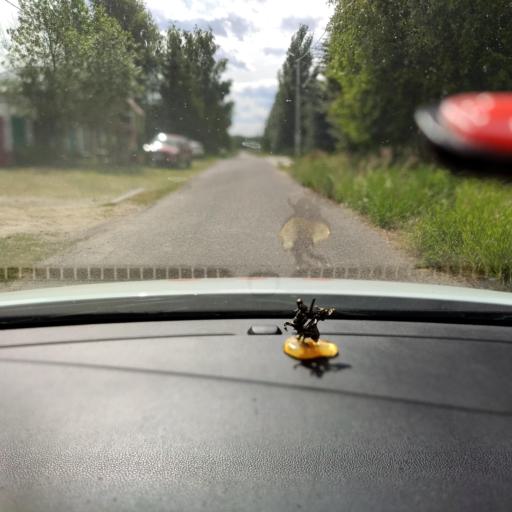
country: RU
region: Tatarstan
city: Stolbishchi
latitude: 55.6341
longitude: 49.1401
